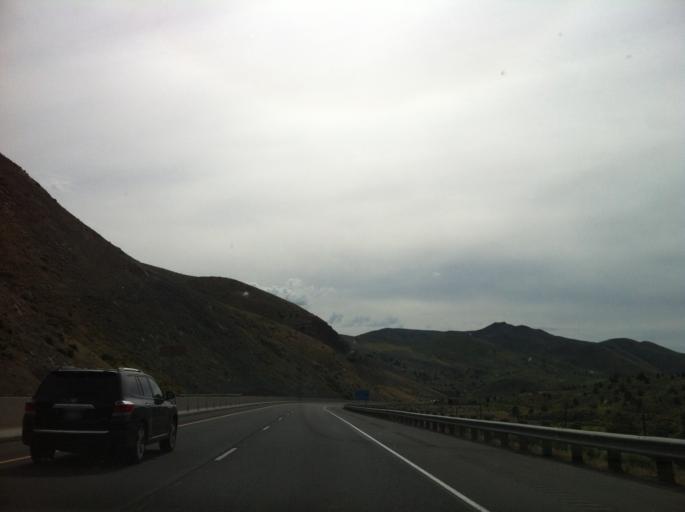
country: US
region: Idaho
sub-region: Washington County
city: Weiser
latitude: 44.5221
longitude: -117.3884
